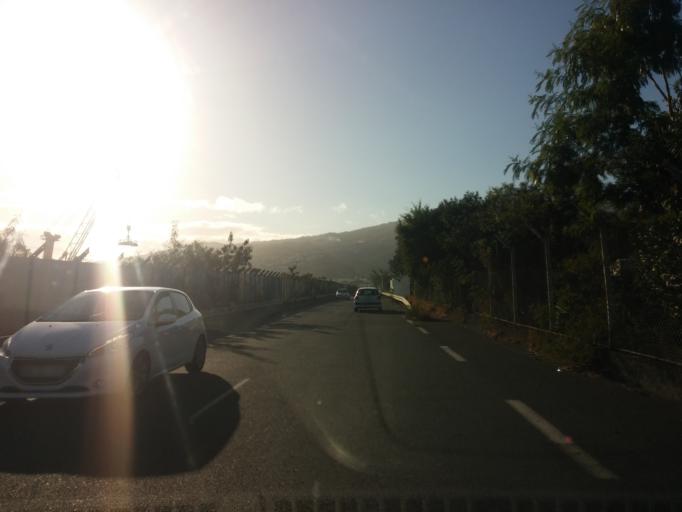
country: RE
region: Reunion
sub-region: Reunion
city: La Possession
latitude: -20.9348
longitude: 55.3156
